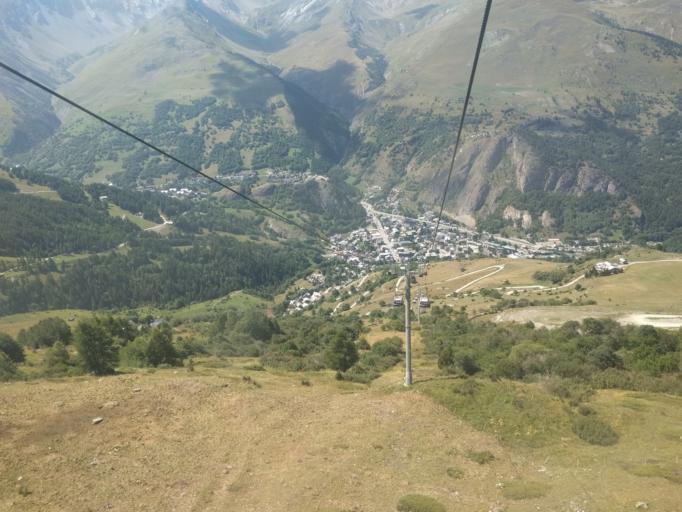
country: FR
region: Rhone-Alpes
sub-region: Departement de la Savoie
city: Valloire
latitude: 45.1624
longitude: 6.4493
